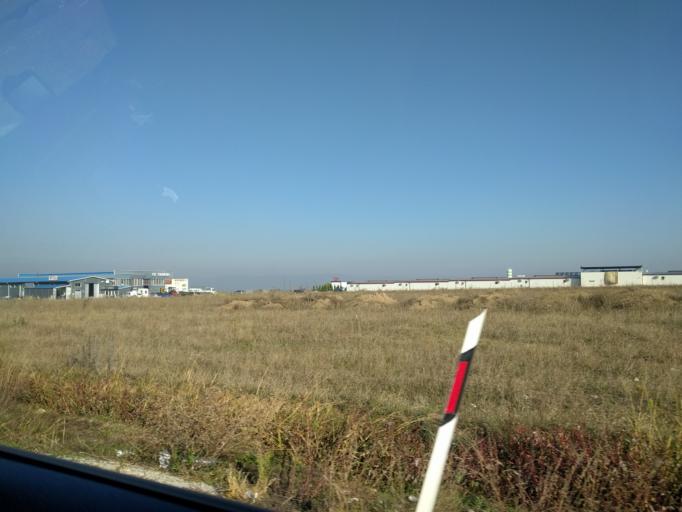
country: XK
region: Prizren
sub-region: Prizren
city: Prizren
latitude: 42.2425
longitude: 20.7502
